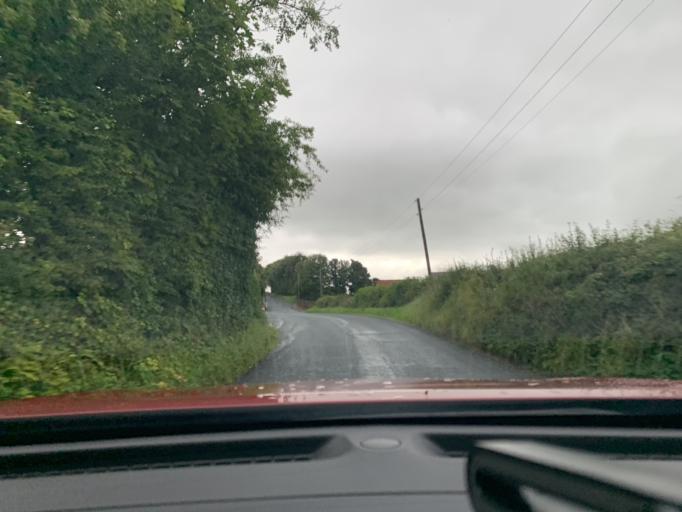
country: IE
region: Connaught
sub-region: Sligo
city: Sligo
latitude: 54.3048
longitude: -8.5135
